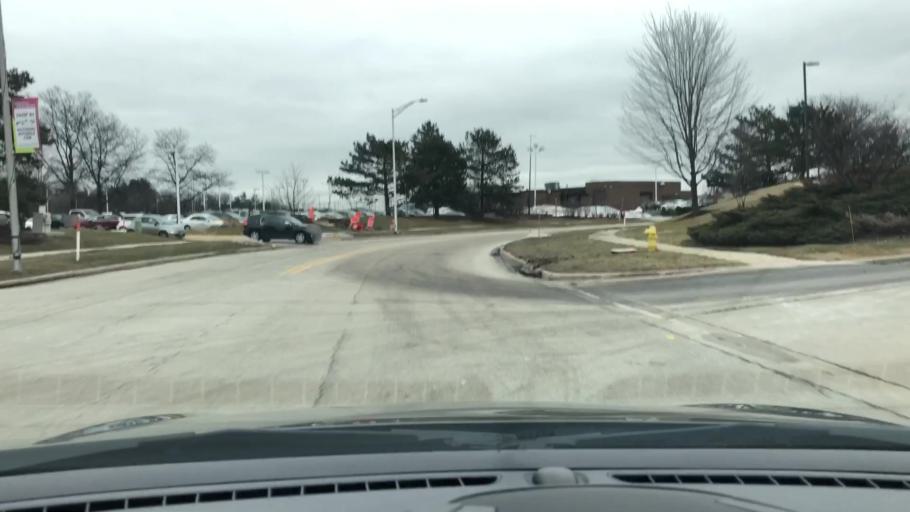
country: US
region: Illinois
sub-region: DuPage County
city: Clarendon Hills
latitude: 41.8145
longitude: -87.9522
